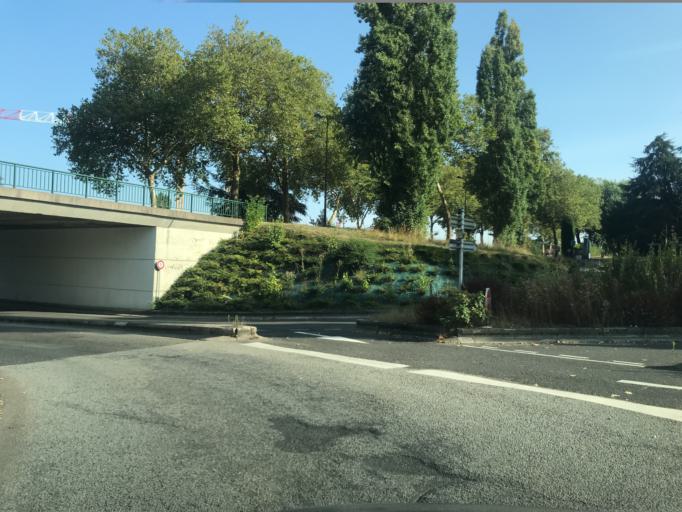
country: FR
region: Ile-de-France
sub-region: Departement des Yvelines
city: Rocquencourt
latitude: 48.8305
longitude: 2.1125
